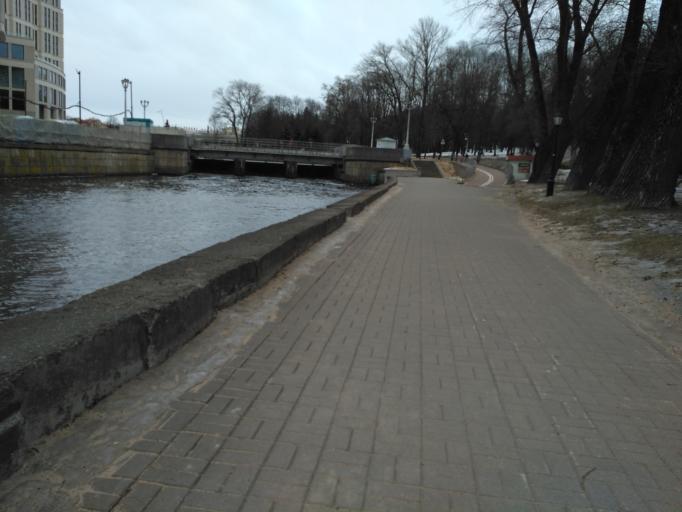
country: BY
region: Minsk
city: Minsk
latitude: 53.9038
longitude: 27.5699
